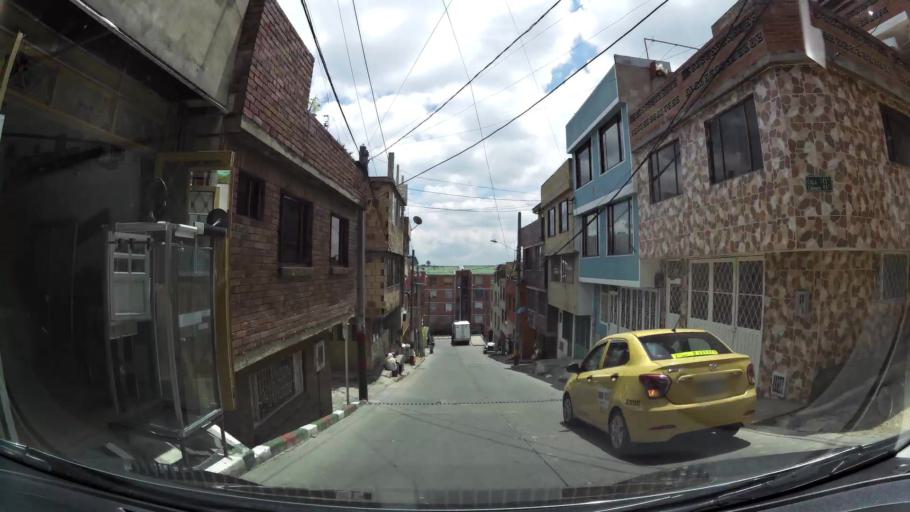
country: CO
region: Cundinamarca
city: Cota
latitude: 4.7373
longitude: -74.0802
